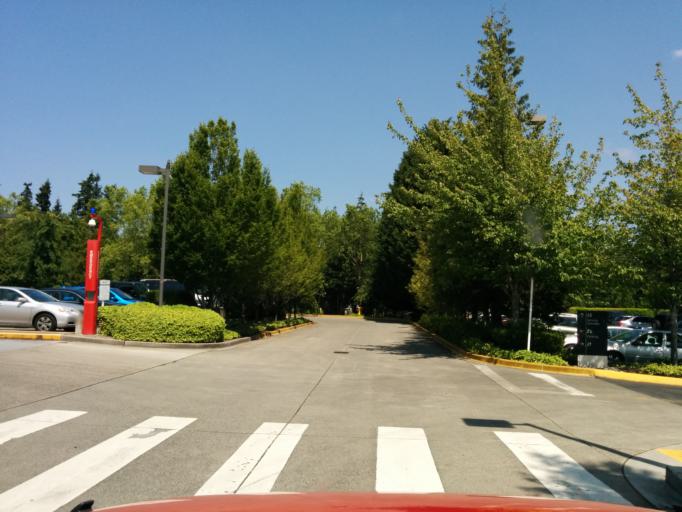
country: US
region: Washington
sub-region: King County
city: Redmond
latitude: 47.6452
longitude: -122.1285
